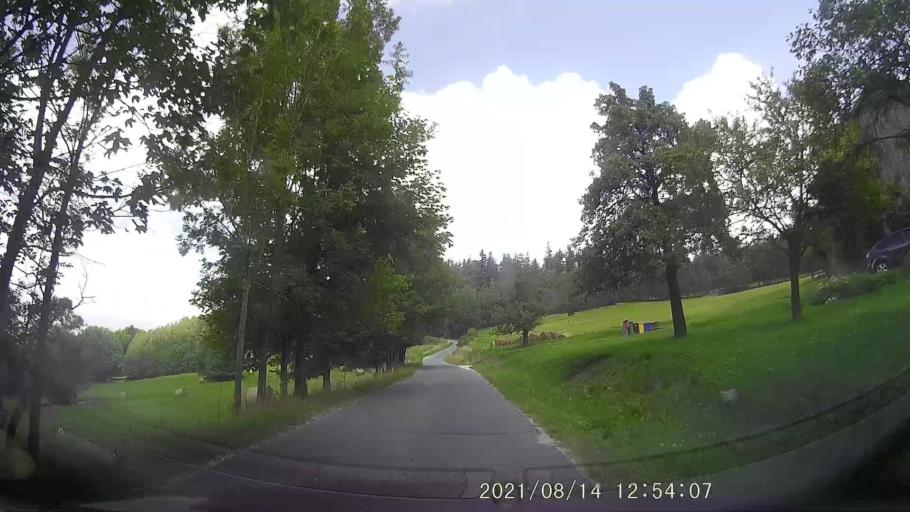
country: PL
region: Lower Silesian Voivodeship
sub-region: Powiat klodzki
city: Stronie Slaskie
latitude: 50.3246
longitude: 16.8247
